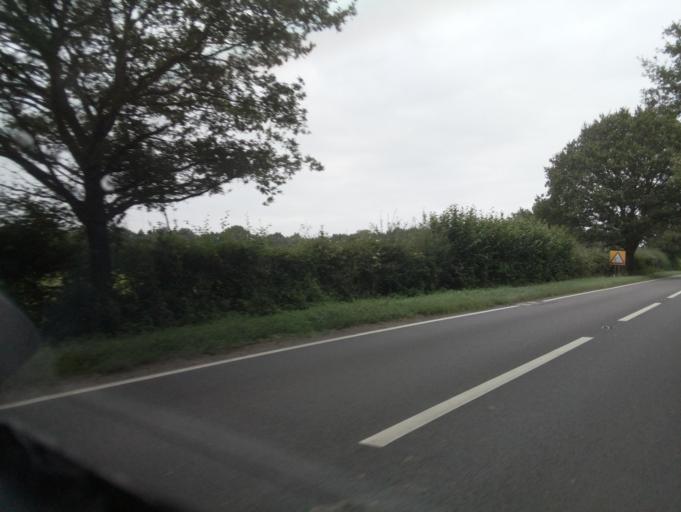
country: GB
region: England
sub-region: Shropshire
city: Astley
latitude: 52.7685
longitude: -2.6773
